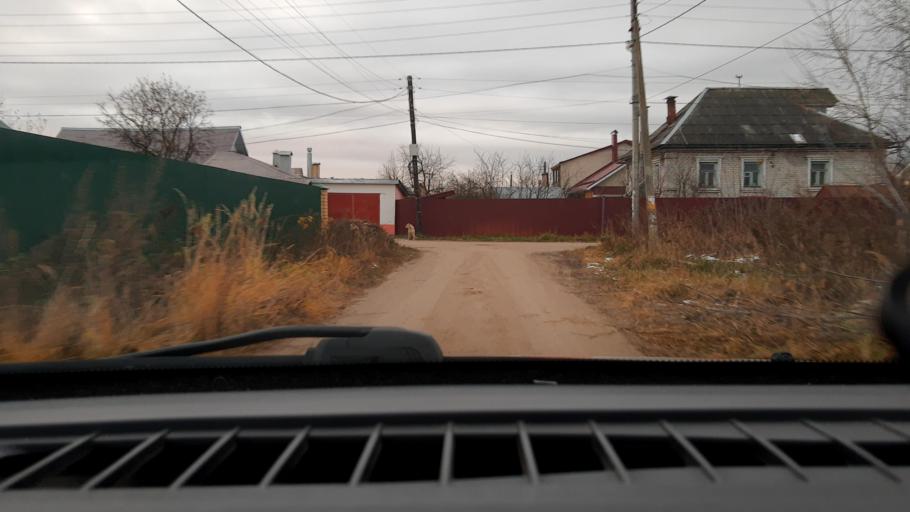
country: RU
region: Nizjnij Novgorod
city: Gorbatovka
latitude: 56.2987
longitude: 43.8509
